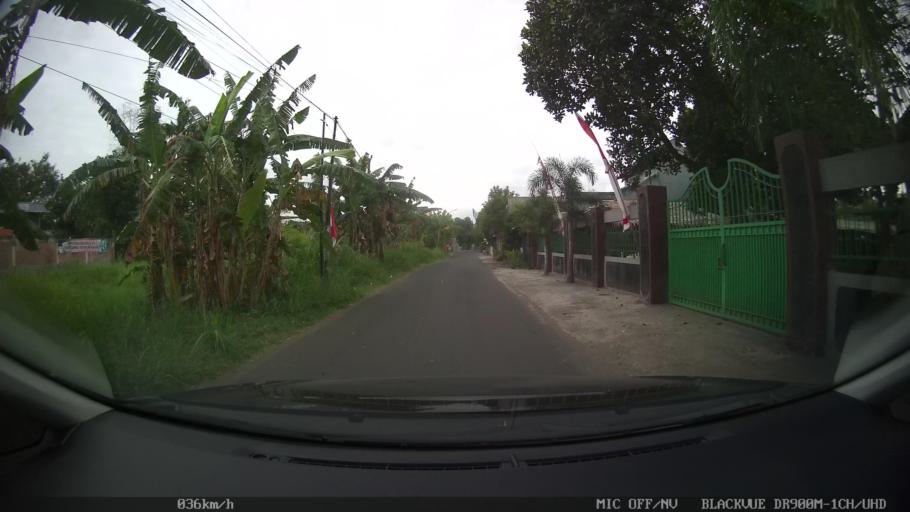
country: ID
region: Daerah Istimewa Yogyakarta
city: Sewon
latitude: -7.8746
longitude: 110.4165
